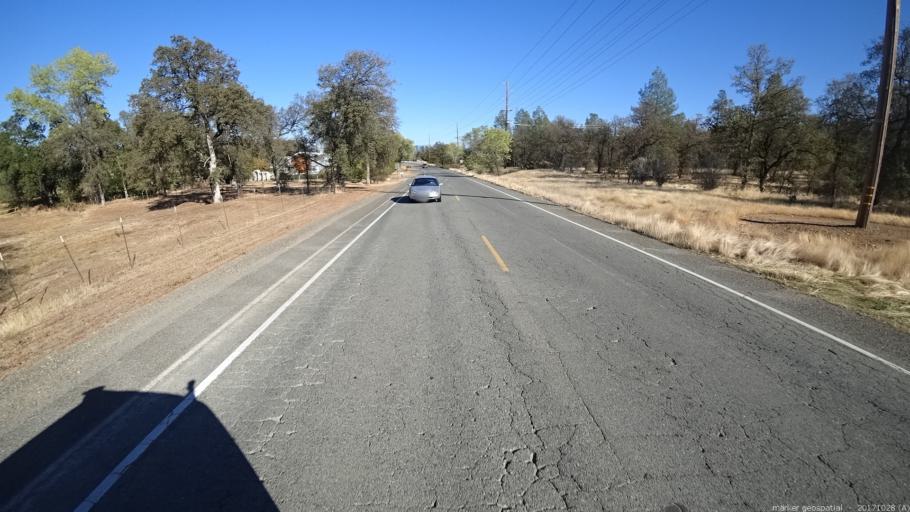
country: US
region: California
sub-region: Shasta County
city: Central Valley (historical)
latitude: 40.6354
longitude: -122.3851
